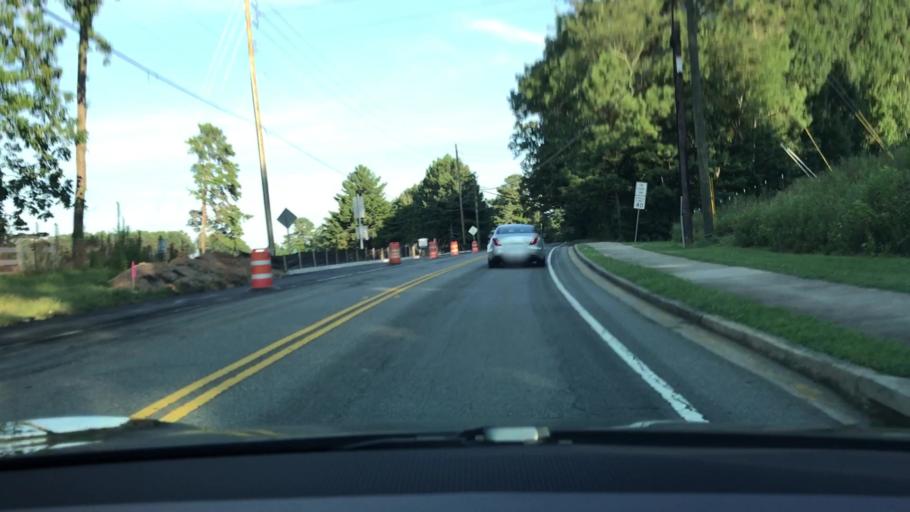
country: US
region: Georgia
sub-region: Fulton County
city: Alpharetta
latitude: 34.0750
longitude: -84.2370
